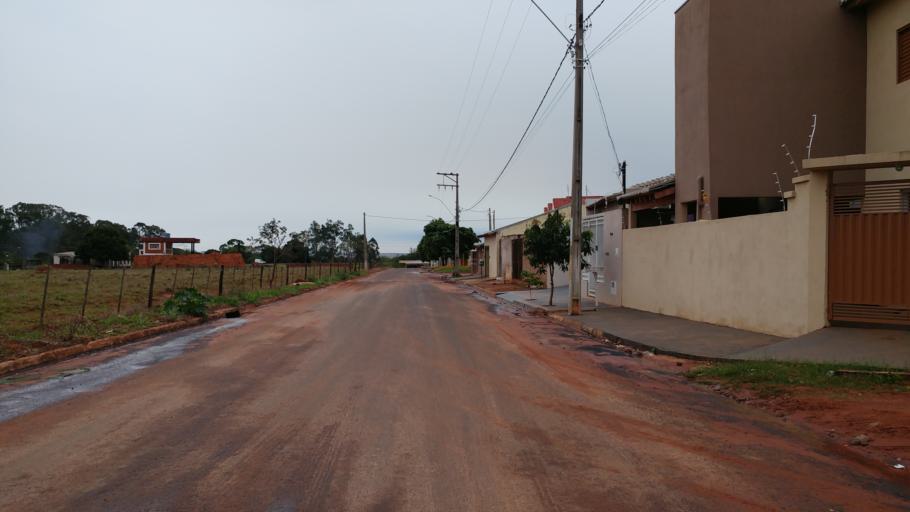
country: BR
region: Sao Paulo
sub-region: Paraguacu Paulista
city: Paraguacu Paulista
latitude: -22.4179
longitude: -50.5906
